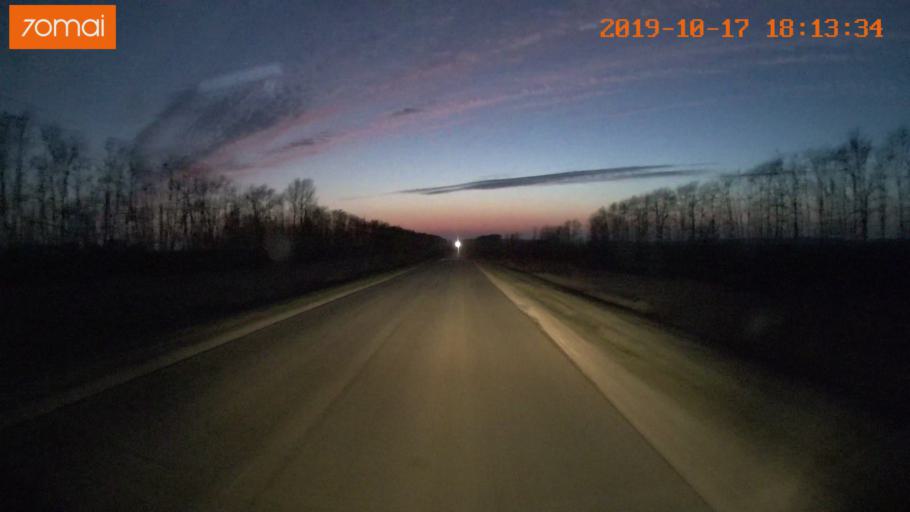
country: RU
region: Tula
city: Kurkino
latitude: 53.4102
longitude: 38.5842
